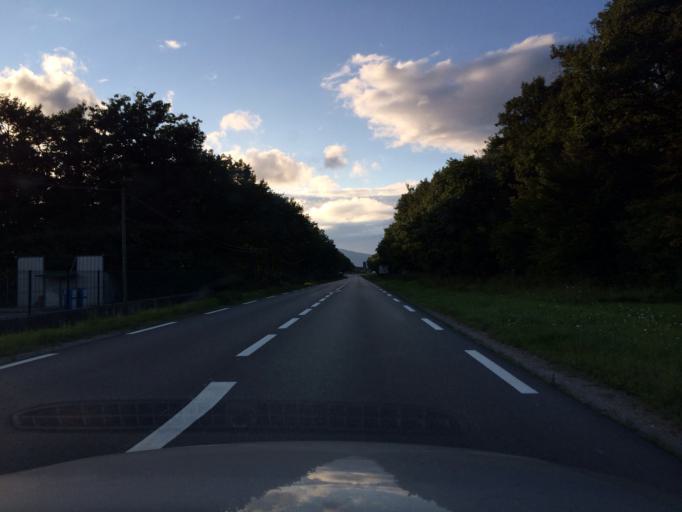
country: FR
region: Rhone-Alpes
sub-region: Departement de l'Ain
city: Bellegarde-sur-Valserine
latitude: 46.0584
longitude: 5.8685
